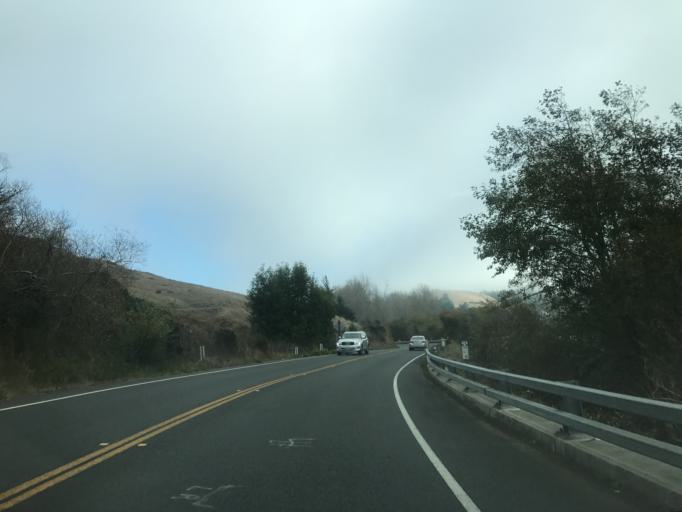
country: US
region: California
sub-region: Sonoma County
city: Monte Rio
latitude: 38.4471
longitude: -123.0610
